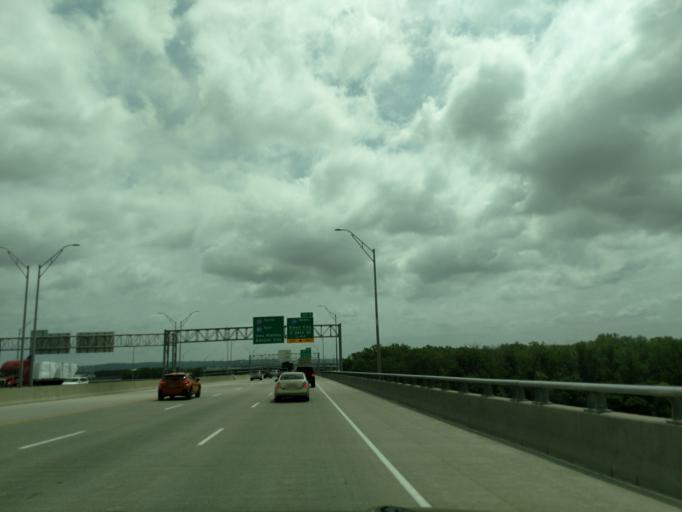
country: US
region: Nebraska
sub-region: Douglas County
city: Omaha
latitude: 41.2315
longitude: -95.9126
